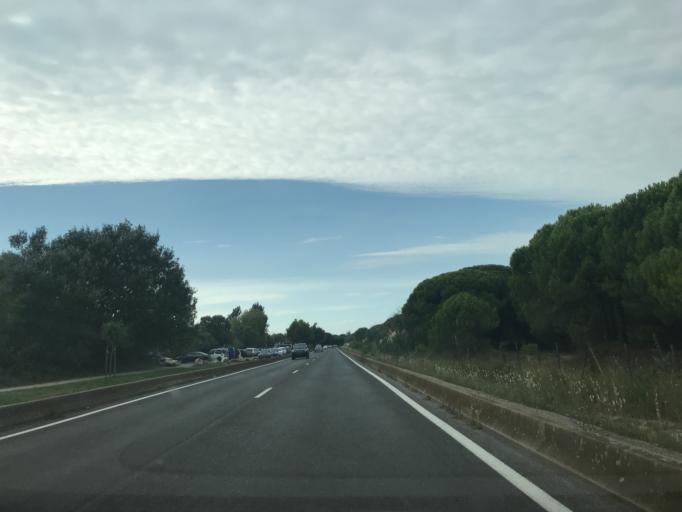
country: FR
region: Languedoc-Roussillon
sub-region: Departement du Gard
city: Le Grau-du-Roi
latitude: 43.5522
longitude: 4.1150
